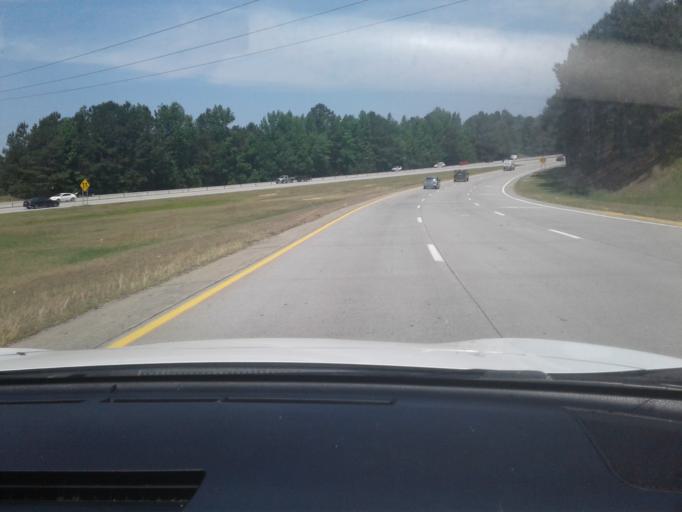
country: US
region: North Carolina
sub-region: Johnston County
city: Benson
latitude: 35.3947
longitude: -78.5211
